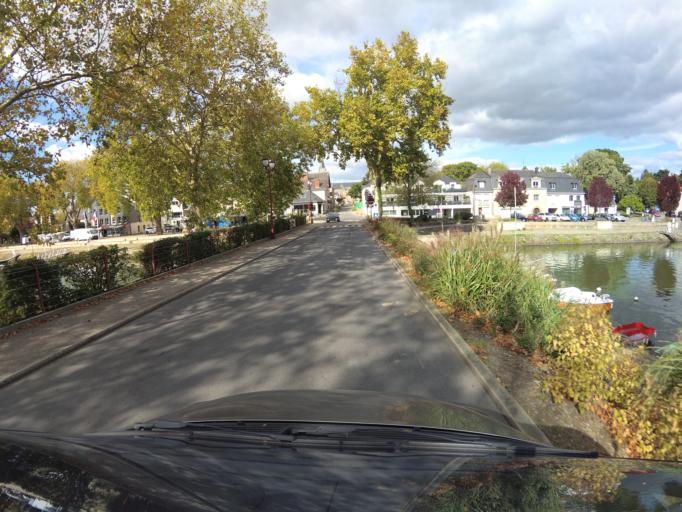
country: FR
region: Pays de la Loire
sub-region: Departement de la Loire-Atlantique
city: Suce-sur-Erdre
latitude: 47.3389
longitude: -1.5258
